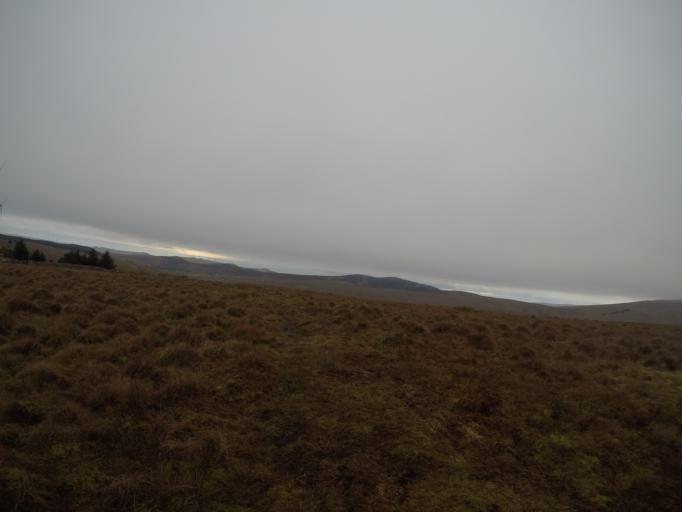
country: GB
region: Scotland
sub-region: North Ayrshire
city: Fairlie
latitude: 55.7371
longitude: -4.7902
